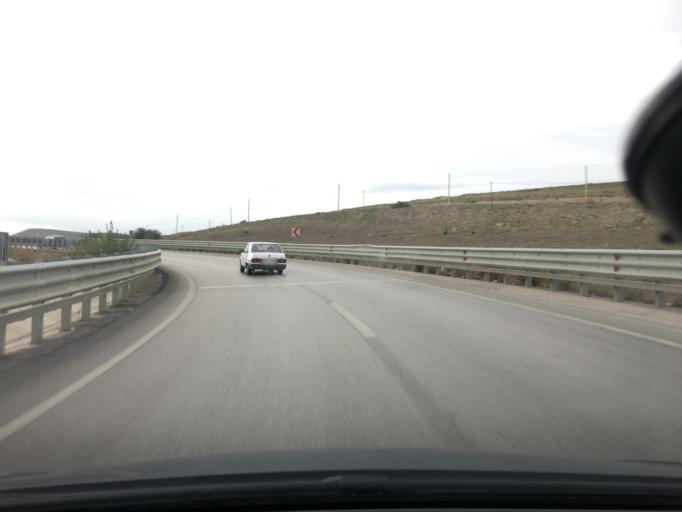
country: TR
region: Afyonkarahisar
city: Afyonkarahisar
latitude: 38.7969
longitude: 30.3916
